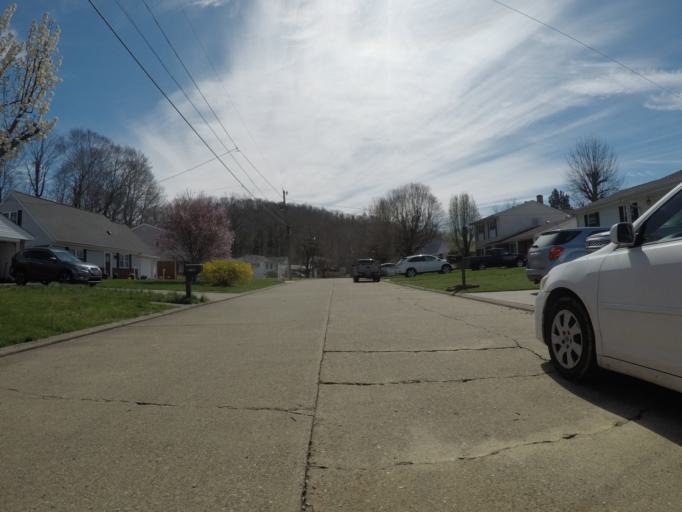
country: US
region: West Virginia
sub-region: Cabell County
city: Pea Ridge
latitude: 38.4012
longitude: -82.3142
